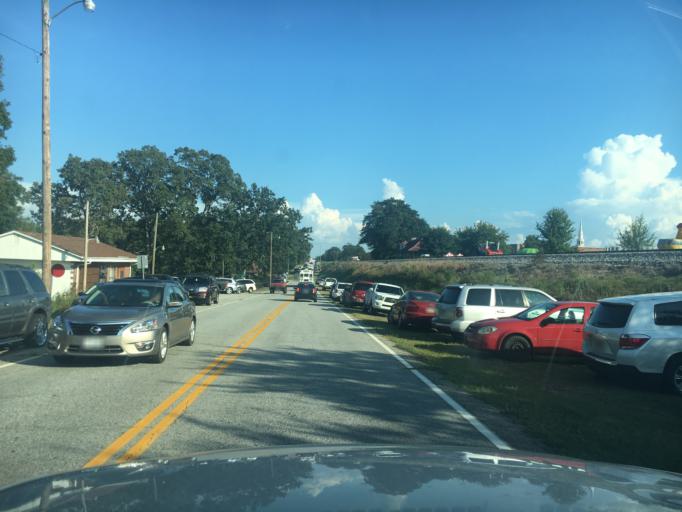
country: US
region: South Carolina
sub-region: Oconee County
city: Westminster
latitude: 34.6673
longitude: -83.0976
